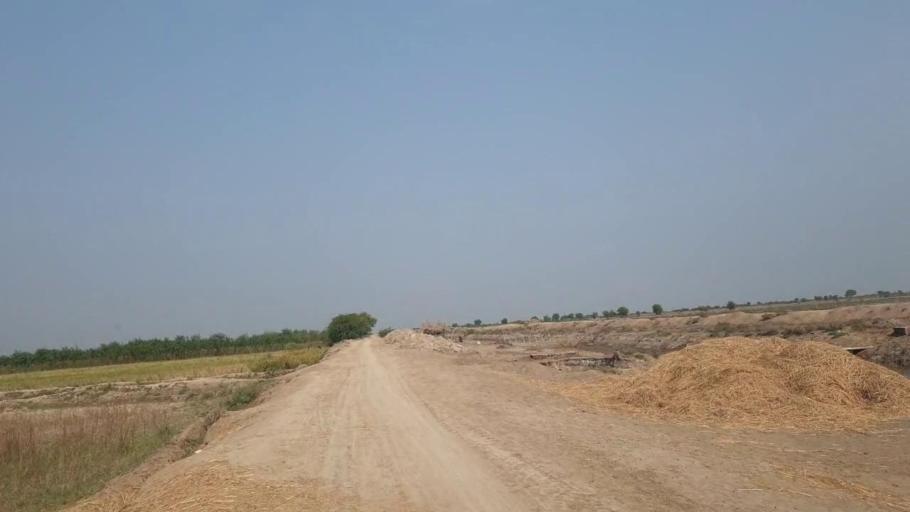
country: PK
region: Sindh
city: Badin
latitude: 24.7228
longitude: 68.7697
